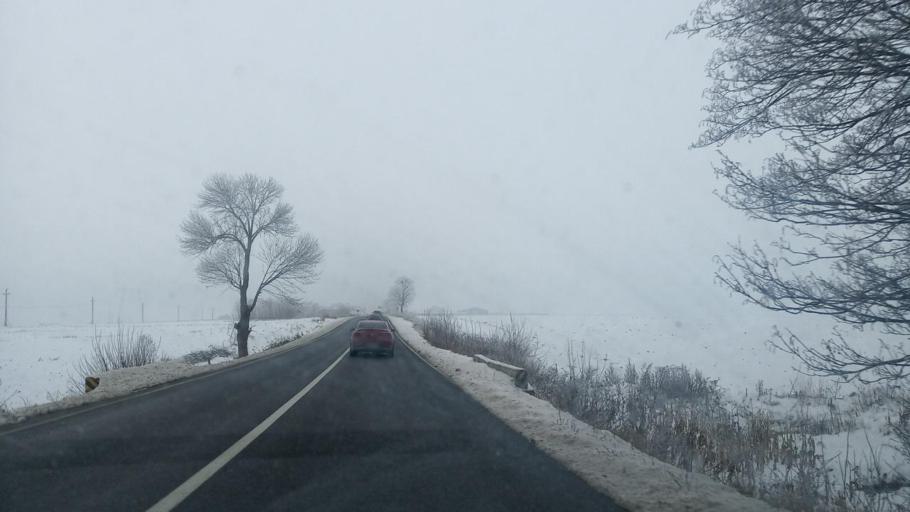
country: RO
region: Neamt
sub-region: Comuna Botesti
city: Nisiporesti
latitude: 47.0936
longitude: 26.7057
